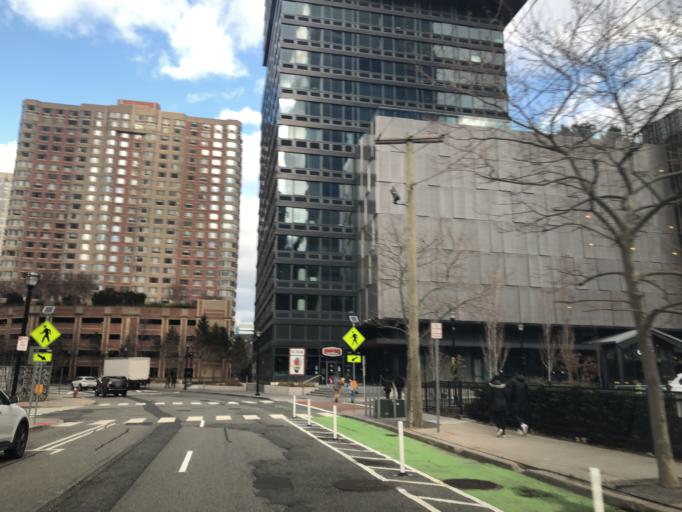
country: US
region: New Jersey
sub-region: Hudson County
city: Hoboken
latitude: 40.7198
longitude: -74.0352
